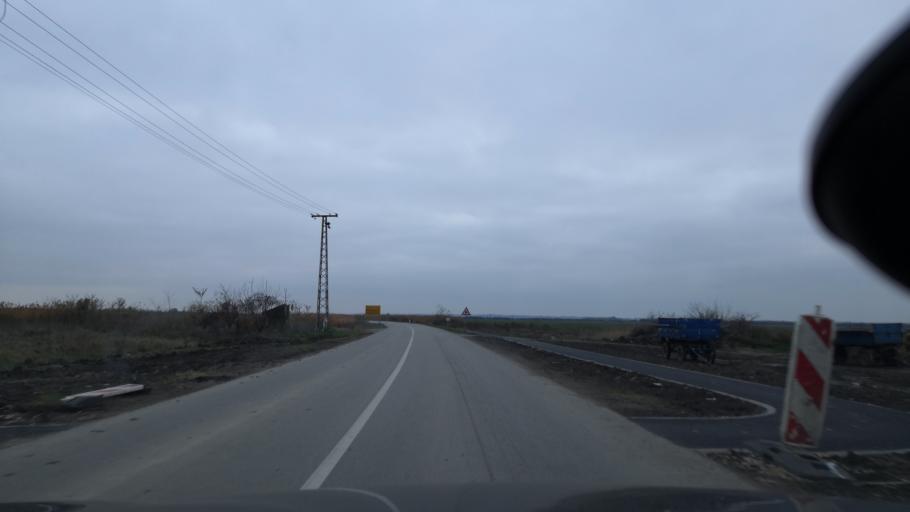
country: RS
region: Autonomna Pokrajina Vojvodina
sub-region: Severnobanatski Okrug
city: Novi Knezevac
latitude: 46.1228
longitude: 20.0982
